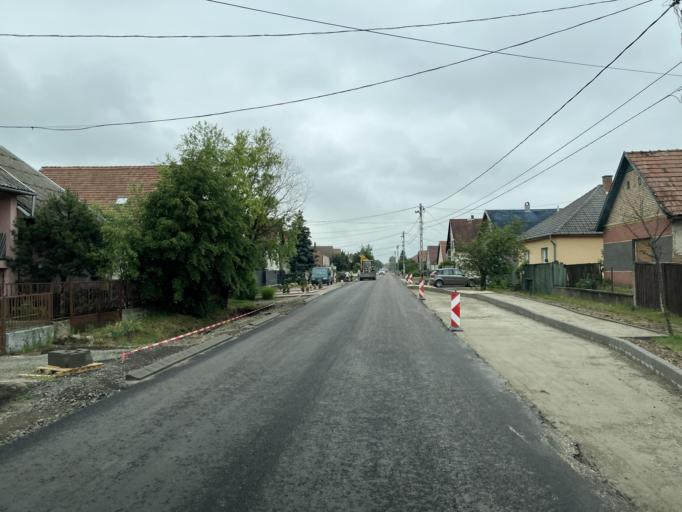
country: HU
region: Pest
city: Galgaheviz
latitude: 47.6152
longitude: 19.5801
